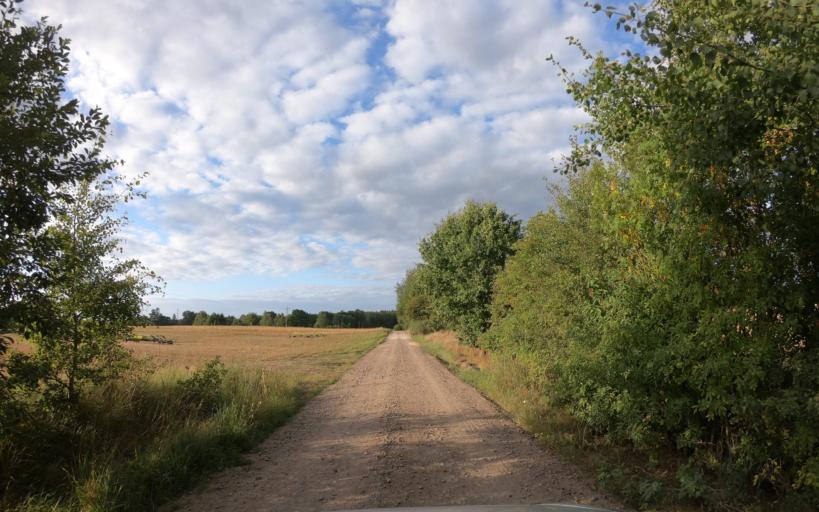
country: PL
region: West Pomeranian Voivodeship
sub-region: Powiat drawski
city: Czaplinek
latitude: 53.5324
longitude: 16.1557
